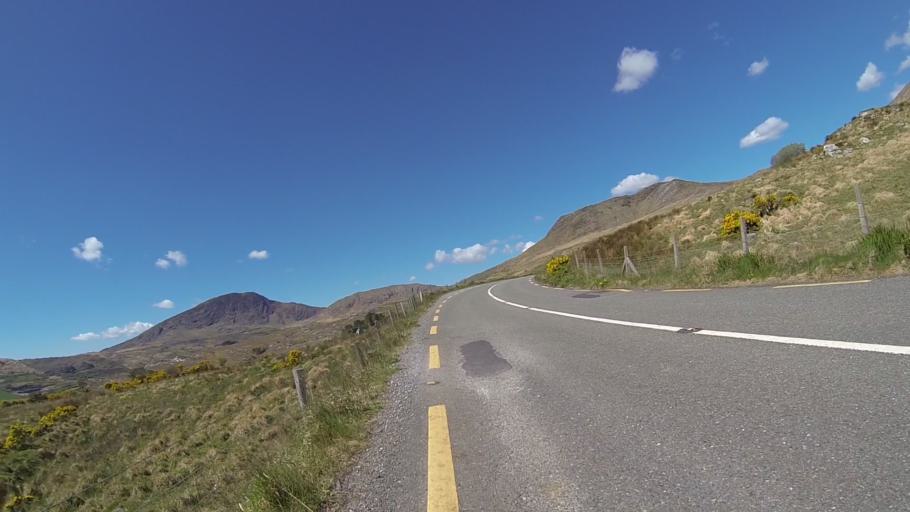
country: IE
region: Munster
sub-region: Ciarrai
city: Kenmare
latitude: 51.9218
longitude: -9.6293
